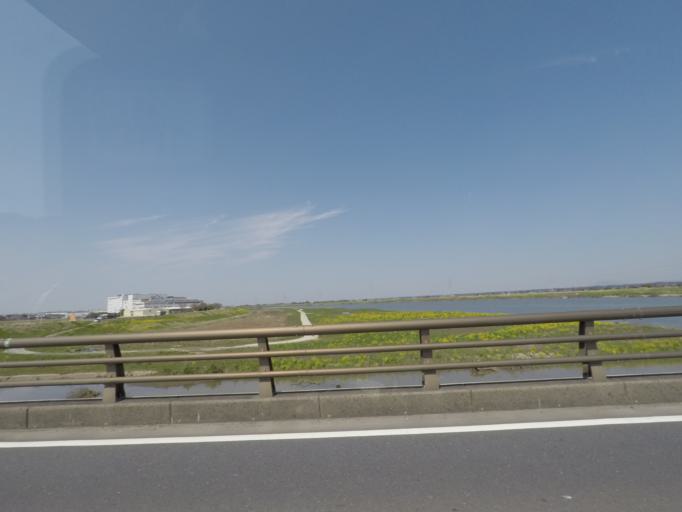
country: JP
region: Ibaraki
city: Edosaki
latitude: 35.8692
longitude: 140.2886
